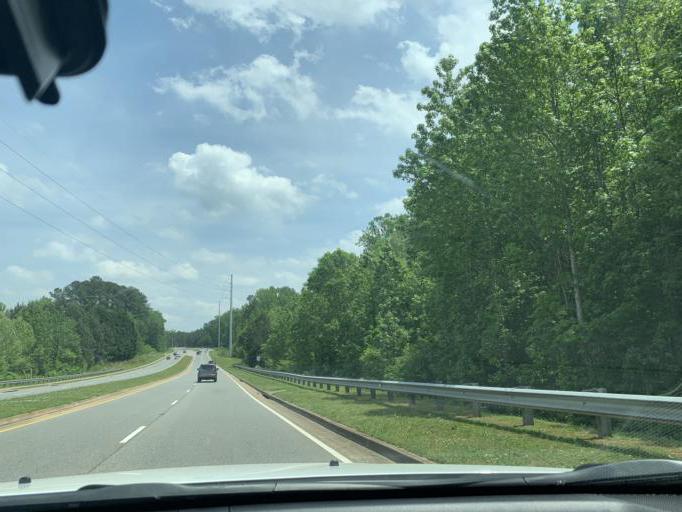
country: US
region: Georgia
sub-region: Forsyth County
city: Cumming
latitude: 34.1551
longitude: -84.1613
